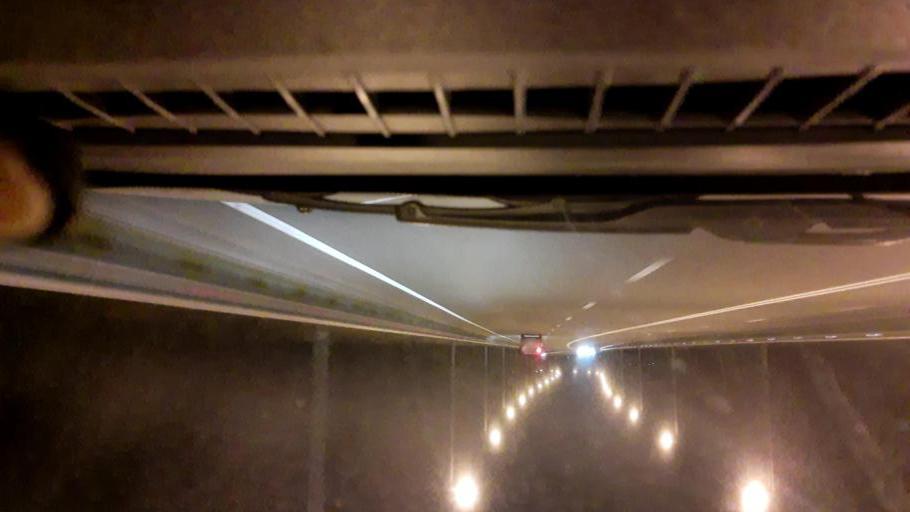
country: RU
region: Nizjnij Novgorod
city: Gorbatovka
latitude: 56.2346
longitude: 43.8069
